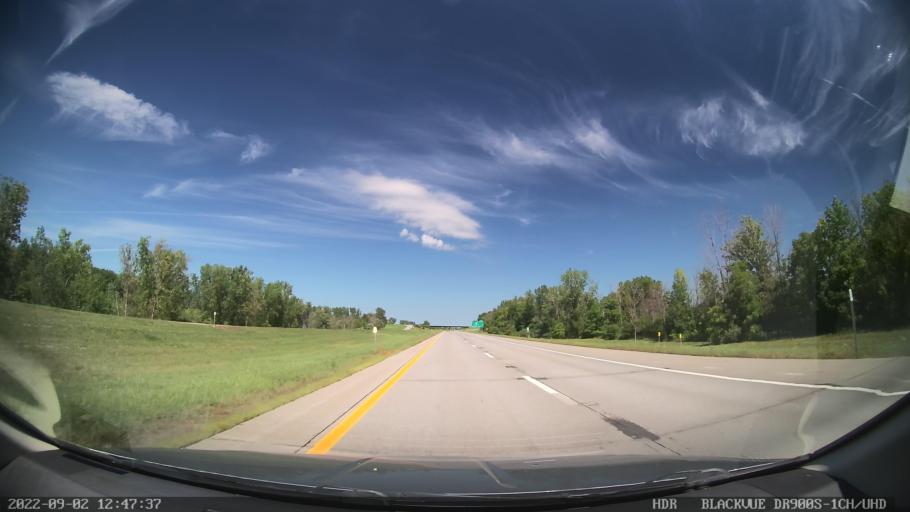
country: US
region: New York
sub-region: Livingston County
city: Livonia
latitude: 42.8185
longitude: -77.7371
